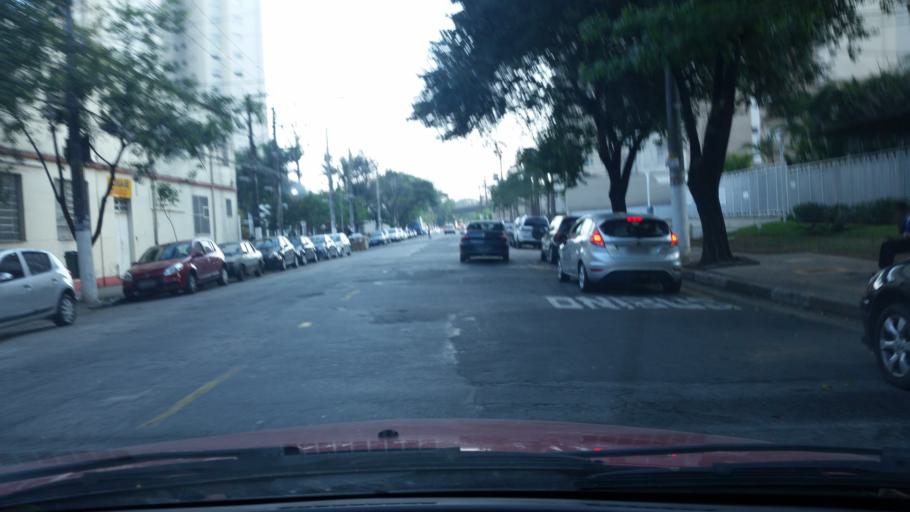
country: BR
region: Sao Paulo
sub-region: Osasco
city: Osasco
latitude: -23.5258
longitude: -46.7385
